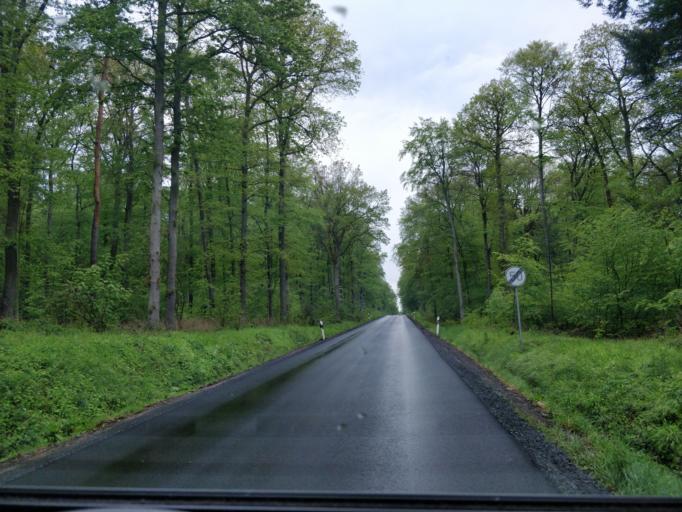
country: DE
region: North Rhine-Westphalia
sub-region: Regierungsbezirk Koln
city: Rheinbach
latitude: 50.6019
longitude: 6.9510
